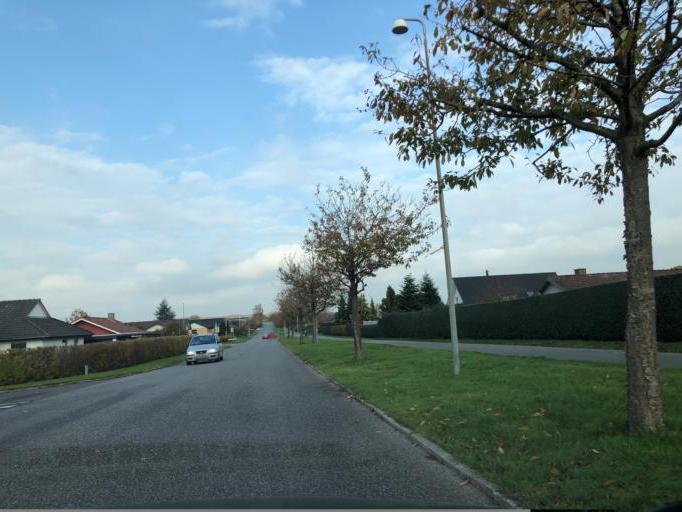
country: DK
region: South Denmark
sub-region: Vejle Kommune
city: Vejle
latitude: 55.7168
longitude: 9.6150
